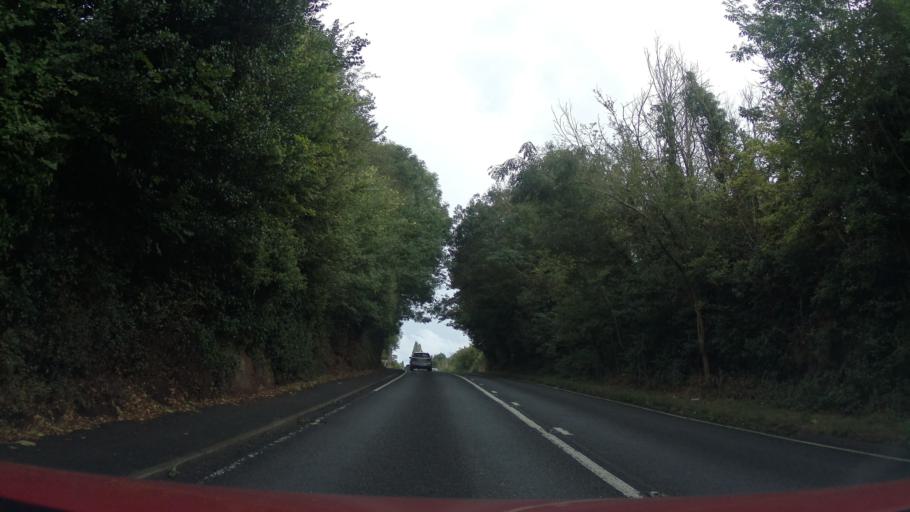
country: GB
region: England
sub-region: Worcestershire
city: Kidderminster
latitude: 52.3736
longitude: -2.2074
